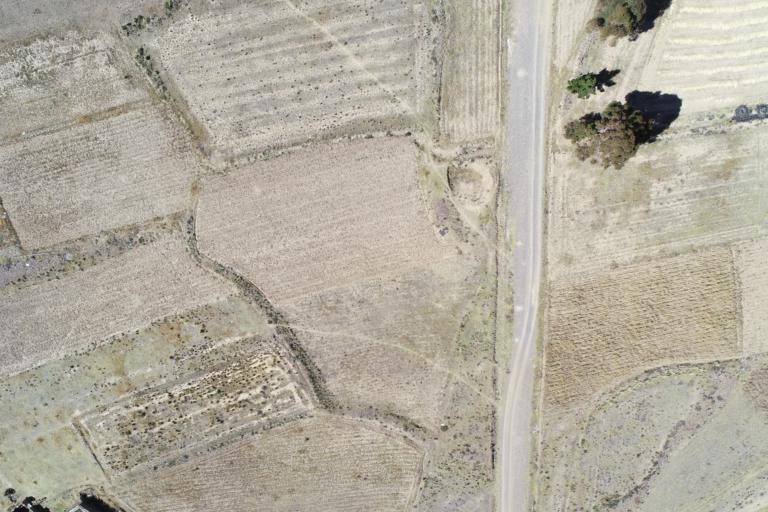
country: BO
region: La Paz
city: Achacachi
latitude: -15.9007
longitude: -68.9021
